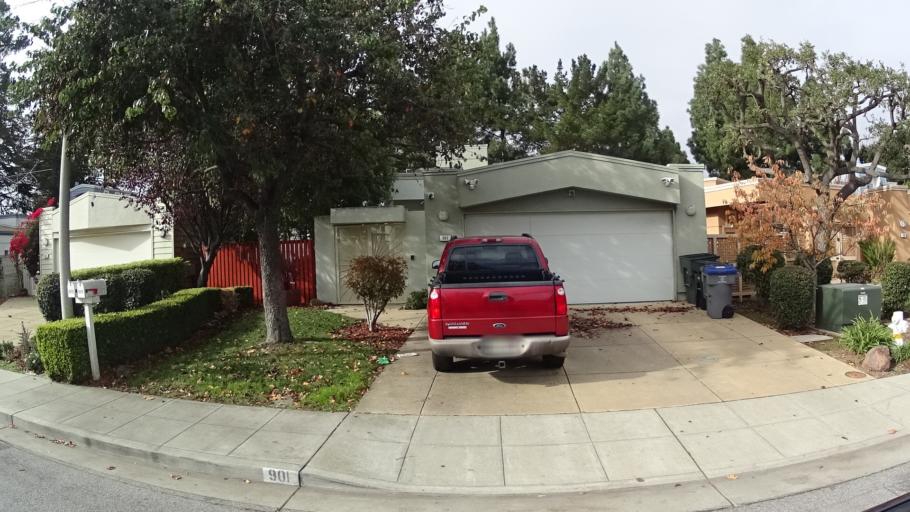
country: US
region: California
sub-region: Santa Clara County
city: Sunnyvale
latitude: 37.3589
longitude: -122.0182
